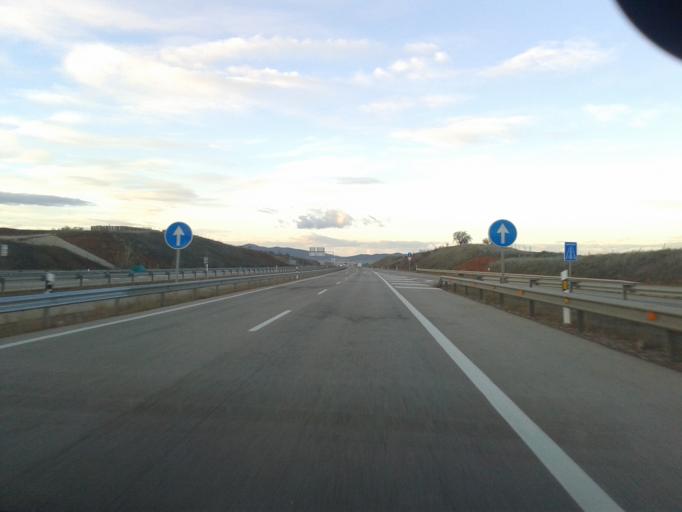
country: ES
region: Aragon
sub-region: Provincia de Zaragoza
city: Romanos
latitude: 41.1225
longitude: -1.2865
